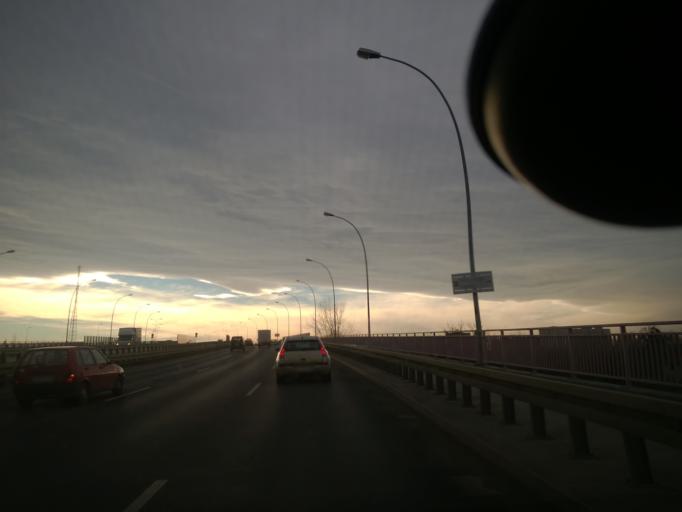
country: PL
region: Lower Silesian Voivodeship
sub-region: Powiat wroclawski
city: Wroclaw
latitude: 51.1181
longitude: 16.9700
